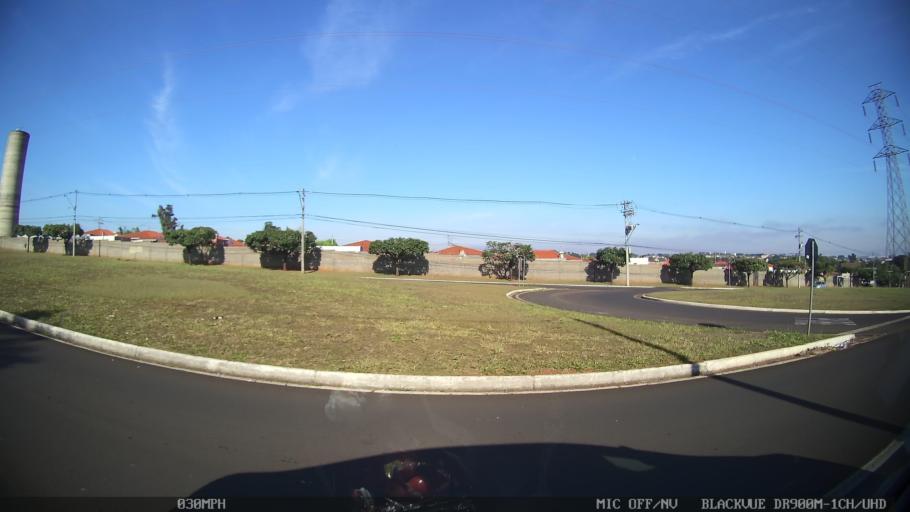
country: BR
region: Sao Paulo
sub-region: Sao Jose Do Rio Preto
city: Sao Jose do Rio Preto
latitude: -20.7754
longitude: -49.3476
